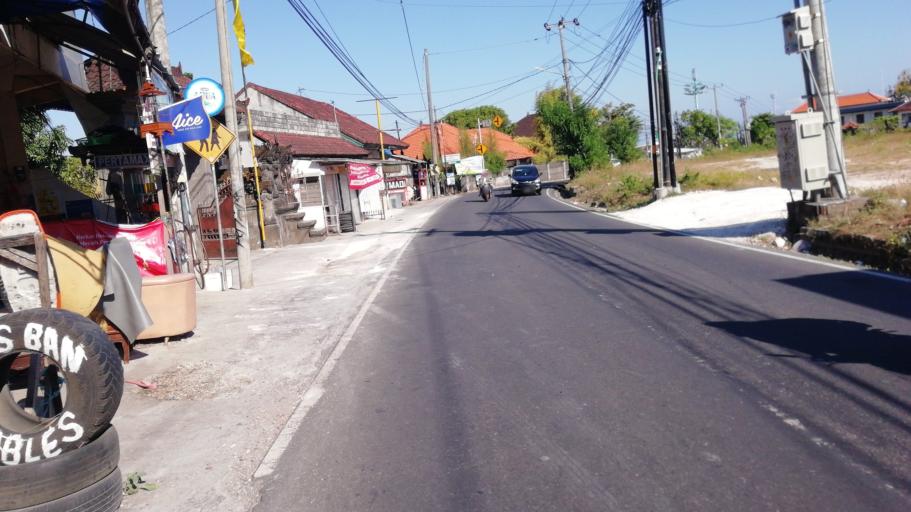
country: ID
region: Bali
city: Jimbaran
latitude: -8.8255
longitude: 115.1658
